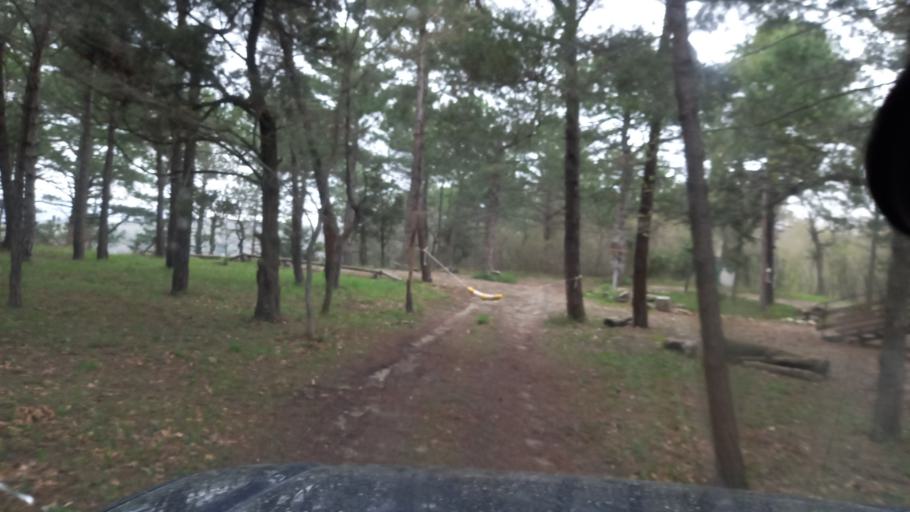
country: RU
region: Krasnodarskiy
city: Dzhubga
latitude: 44.3171
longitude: 38.6638
